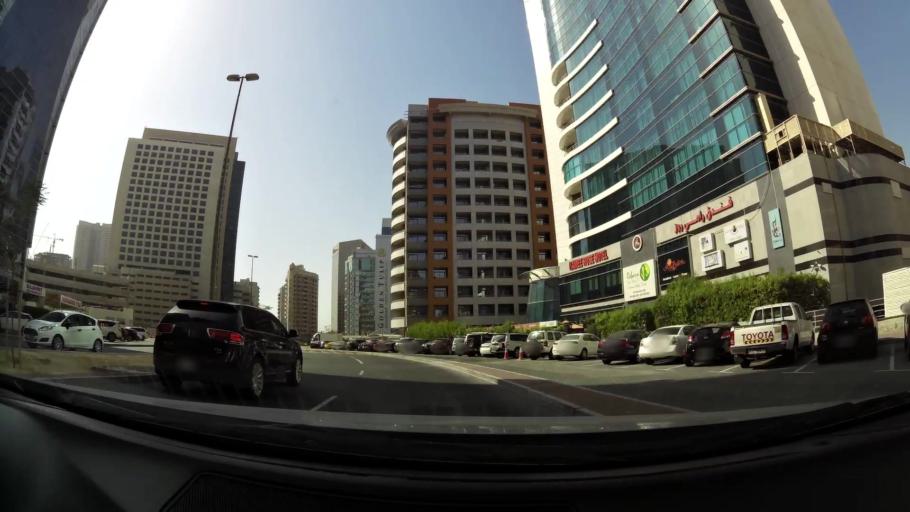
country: AE
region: Dubai
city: Dubai
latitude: 25.0978
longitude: 55.1794
